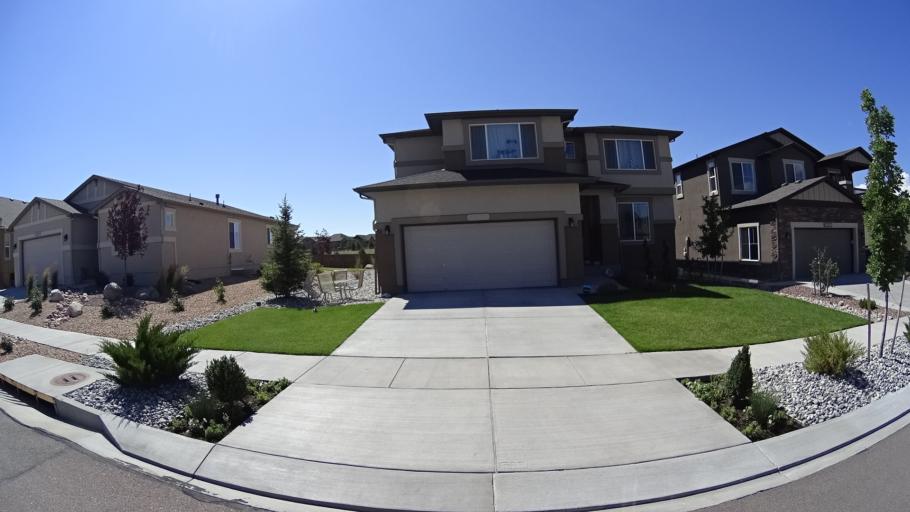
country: US
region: Colorado
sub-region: El Paso County
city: Black Forest
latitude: 38.9788
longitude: -104.7465
